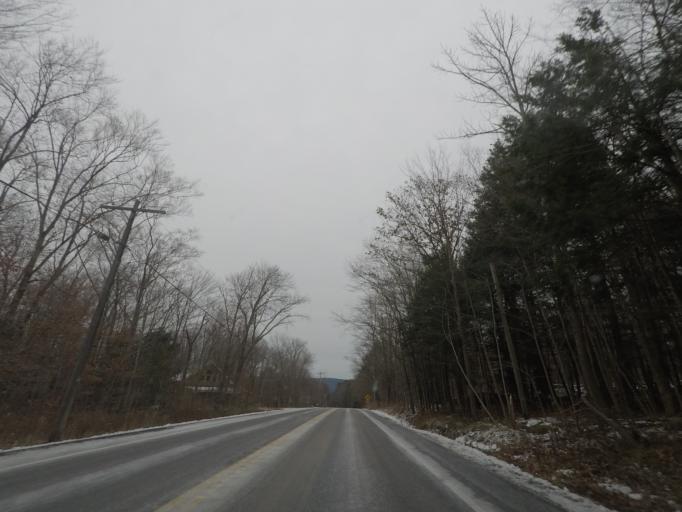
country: US
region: New York
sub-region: Rensselaer County
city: Hoosick Falls
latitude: 42.7644
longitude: -73.3997
